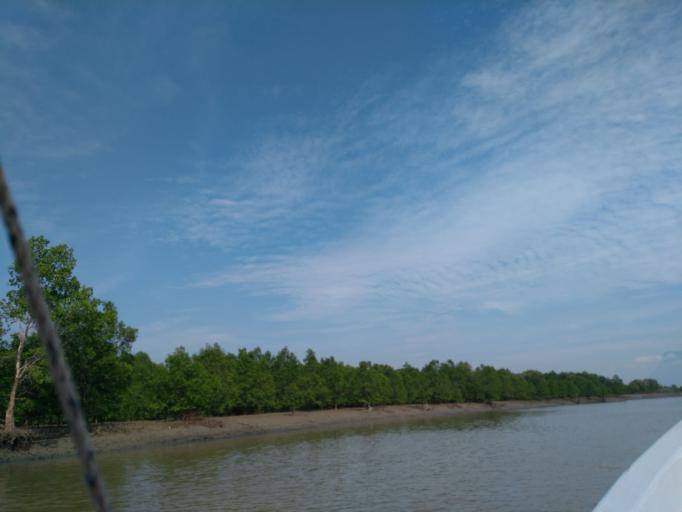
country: MY
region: Sarawak
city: Kuching
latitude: 1.6770
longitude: 110.4271
